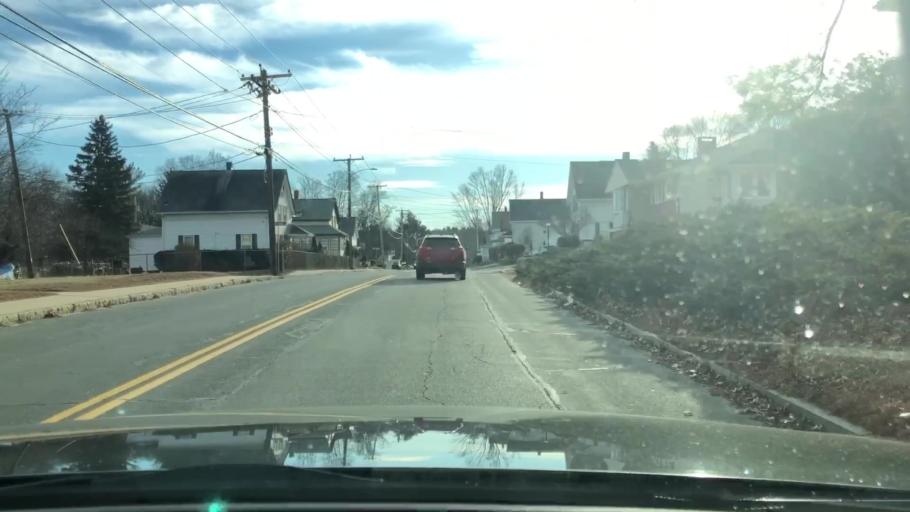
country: US
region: Massachusetts
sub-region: Worcester County
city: Milford
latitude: 42.1353
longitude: -71.5149
